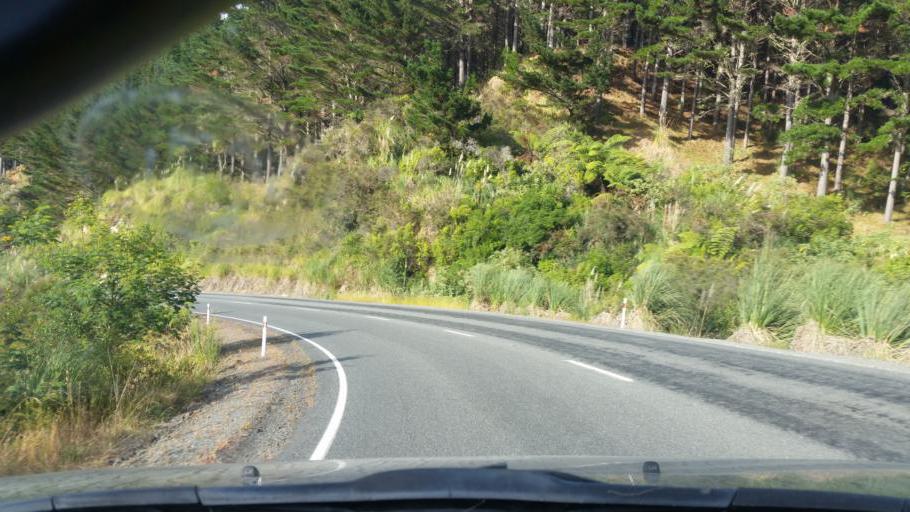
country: NZ
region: Northland
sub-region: Kaipara District
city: Dargaville
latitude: -36.2231
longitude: 174.0379
